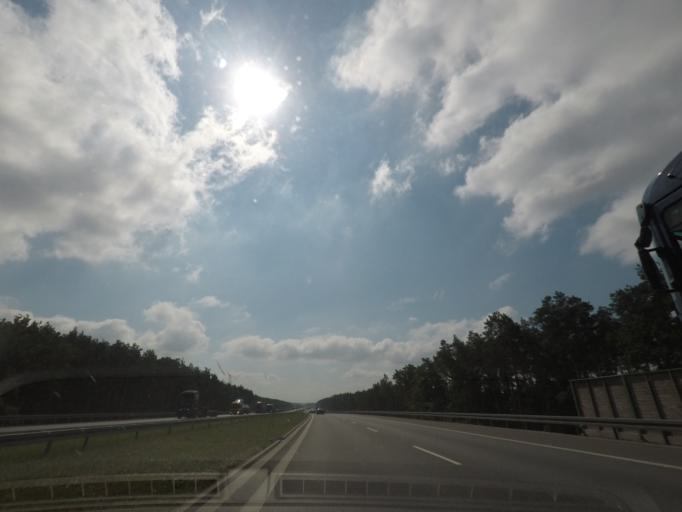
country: PL
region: Kujawsko-Pomorskie
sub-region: Powiat aleksandrowski
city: Aleksandrow Kujawski
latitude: 52.8908
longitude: 18.7295
